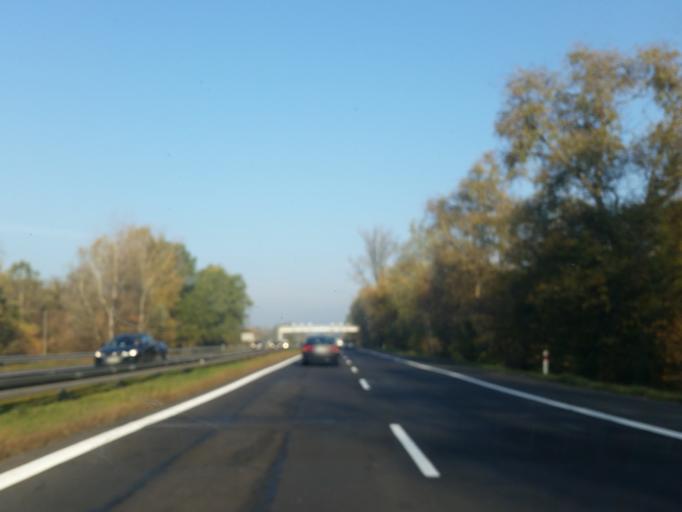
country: PL
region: Masovian Voivodeship
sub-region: Powiat nowodworski
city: Nowy Dwor Mazowiecki
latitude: 52.4040
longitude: 20.7068
